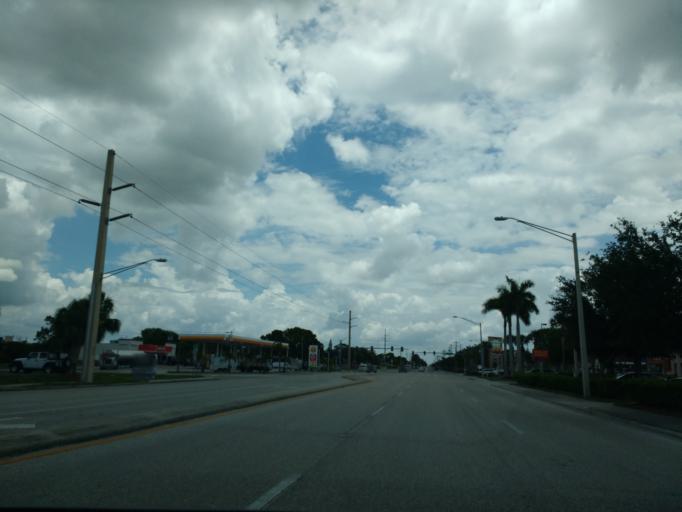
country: US
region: Florida
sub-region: Lee County
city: Cape Coral
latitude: 26.5627
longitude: -82.0084
